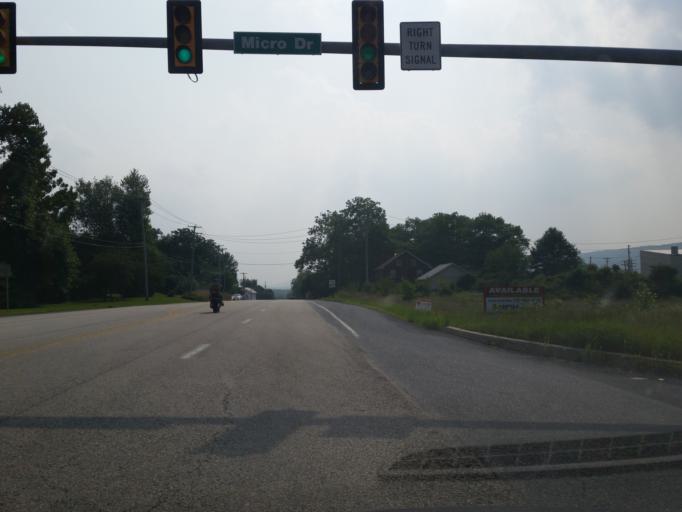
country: US
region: Pennsylvania
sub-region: Lebanon County
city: Jonestown
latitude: 40.4451
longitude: -76.5278
